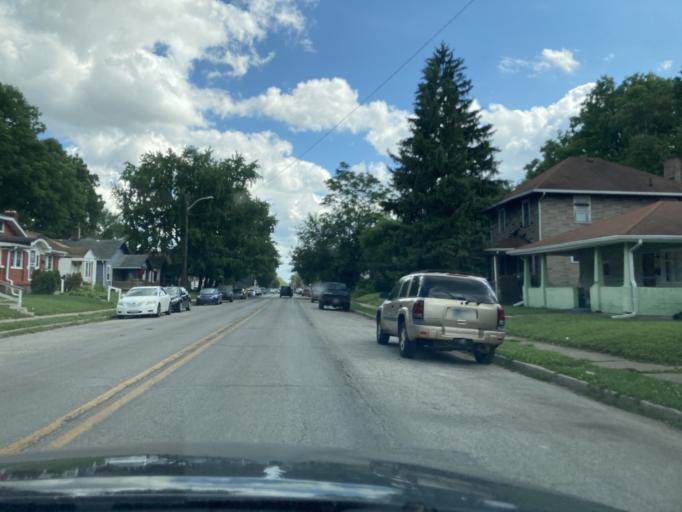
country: US
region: Indiana
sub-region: Marion County
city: Broad Ripple
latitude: 39.8303
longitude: -86.1640
